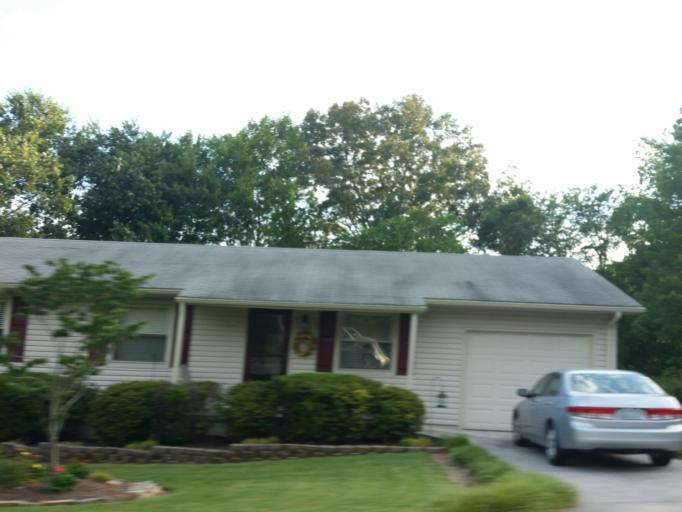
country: US
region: Tennessee
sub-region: Knox County
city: Knoxville
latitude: 36.0436
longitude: -83.9386
